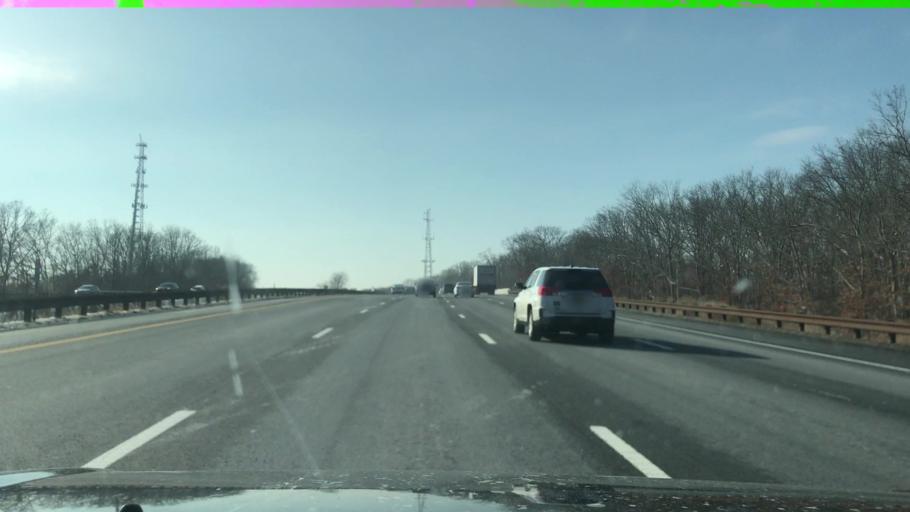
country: US
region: New Jersey
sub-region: Monmouth County
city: Ramtown
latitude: 40.1338
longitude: -74.1188
